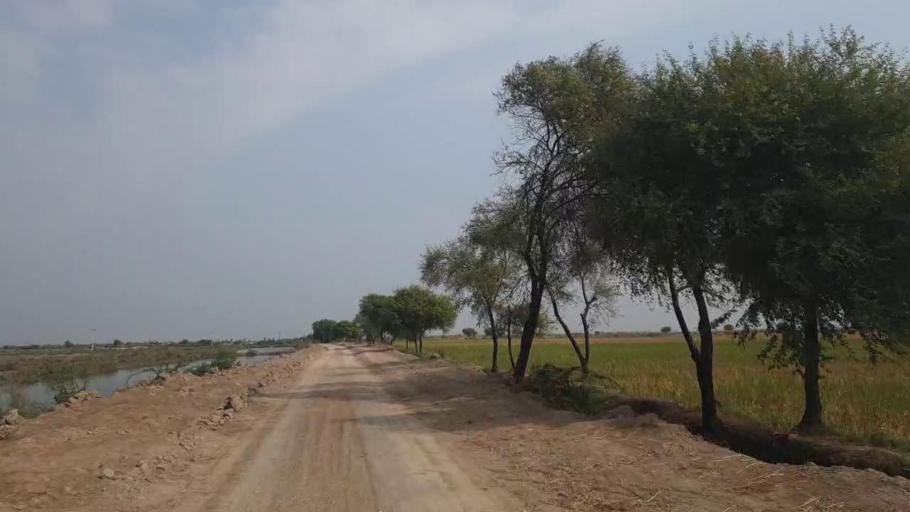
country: PK
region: Sindh
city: Badin
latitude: 24.6191
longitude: 68.7434
